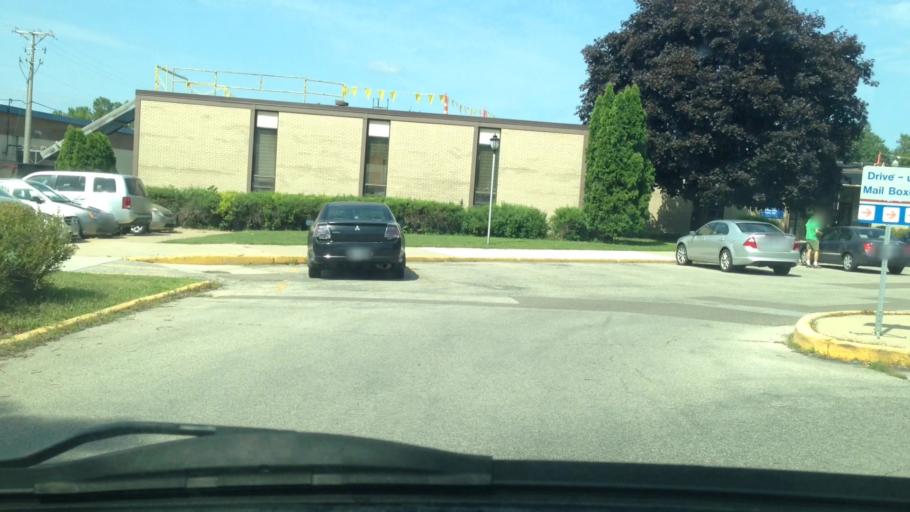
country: US
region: Minnesota
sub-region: Olmsted County
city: Rochester
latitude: 44.0373
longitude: -92.4916
